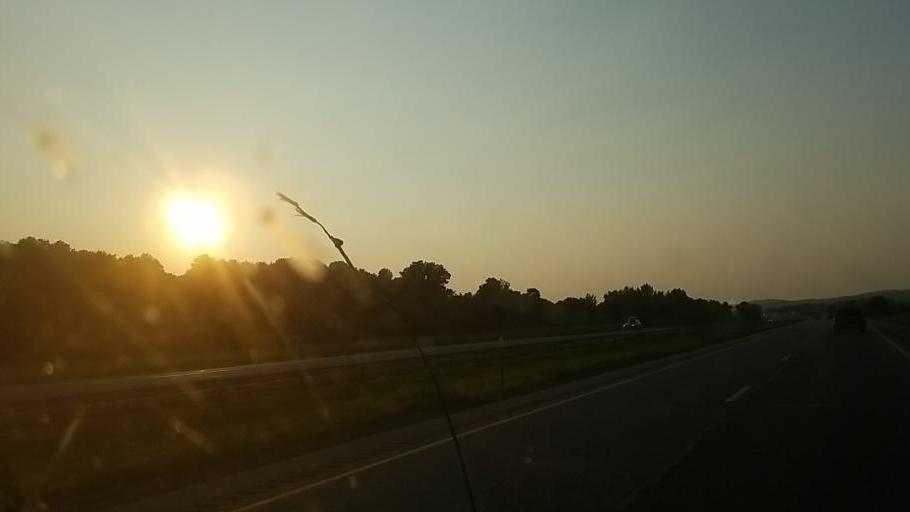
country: US
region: New York
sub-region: Montgomery County
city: Saint Johnsville
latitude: 42.9714
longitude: -74.6481
